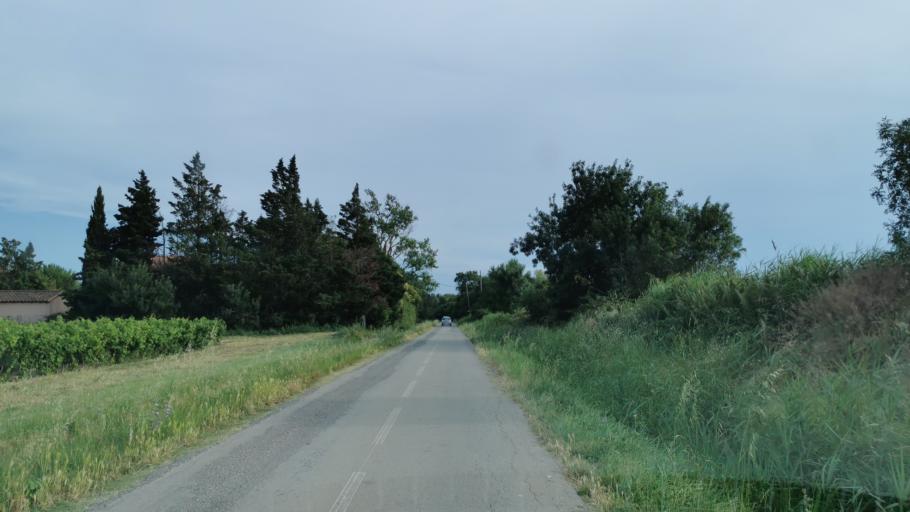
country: FR
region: Languedoc-Roussillon
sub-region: Departement de l'Aude
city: Narbonne
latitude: 43.2107
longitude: 2.9992
